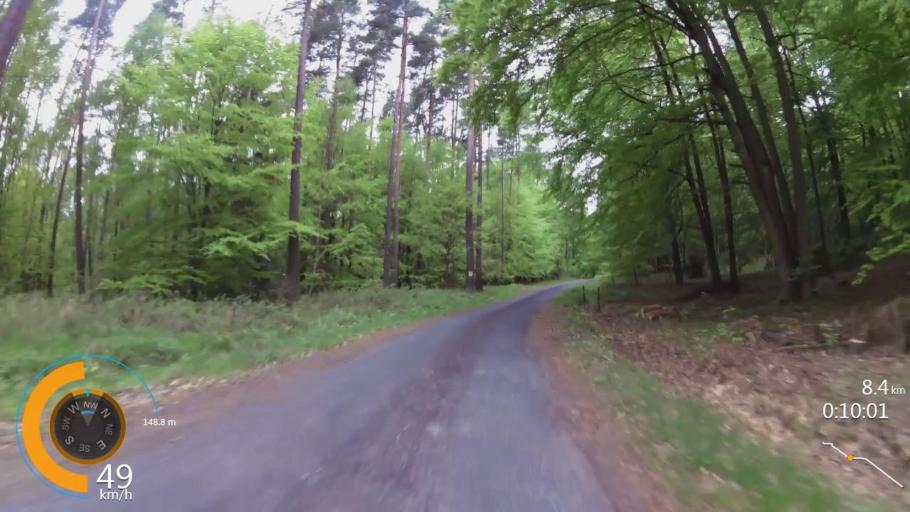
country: PL
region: West Pomeranian Voivodeship
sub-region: Powiat drawski
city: Wierzchowo
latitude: 53.5041
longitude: 16.1279
